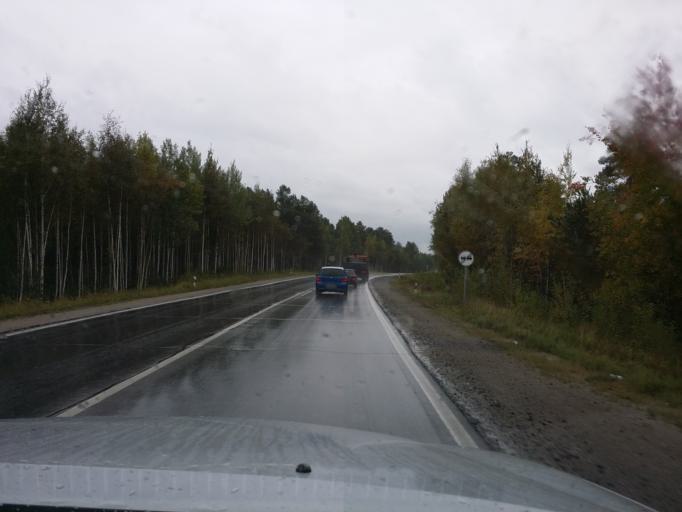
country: RU
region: Khanty-Mansiyskiy Avtonomnyy Okrug
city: Megion
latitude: 61.1582
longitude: 75.7311
